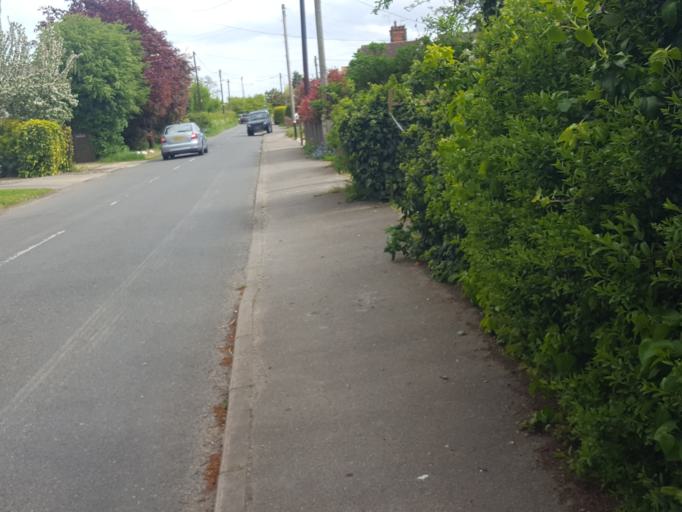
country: GB
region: England
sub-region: Essex
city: Frinton-on-Sea
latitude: 51.8335
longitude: 1.2078
